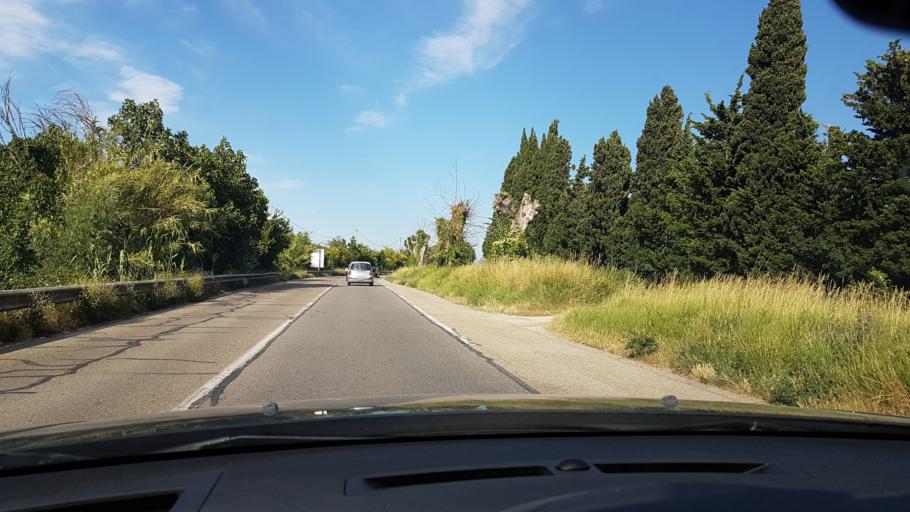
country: FR
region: Provence-Alpes-Cote d'Azur
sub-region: Departement des Bouches-du-Rhone
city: Graveson
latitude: 43.8475
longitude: 4.7538
